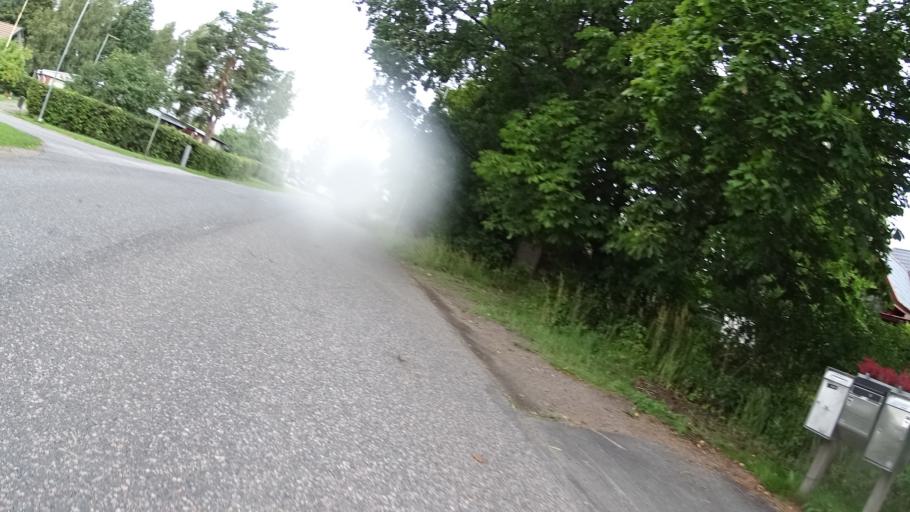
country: FI
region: Uusimaa
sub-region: Helsinki
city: Vantaa
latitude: 60.2909
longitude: 25.0063
